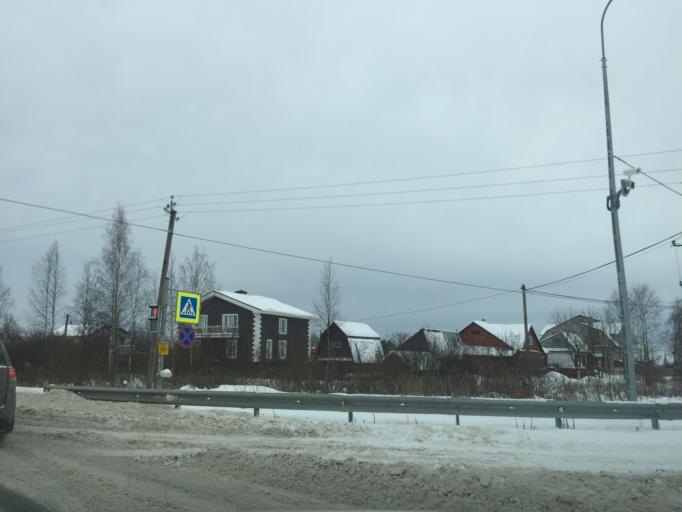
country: RU
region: Leningrad
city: Imeni Sverdlova
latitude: 59.7966
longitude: 30.6659
